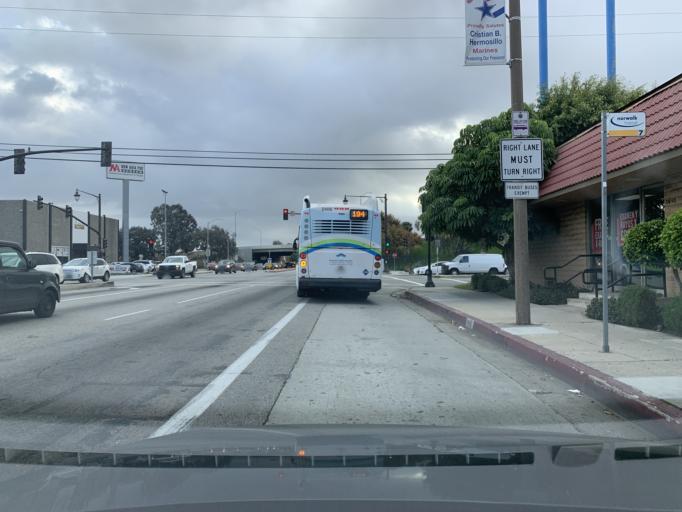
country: US
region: California
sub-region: Los Angeles County
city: El Monte
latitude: 34.0692
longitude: -118.0286
